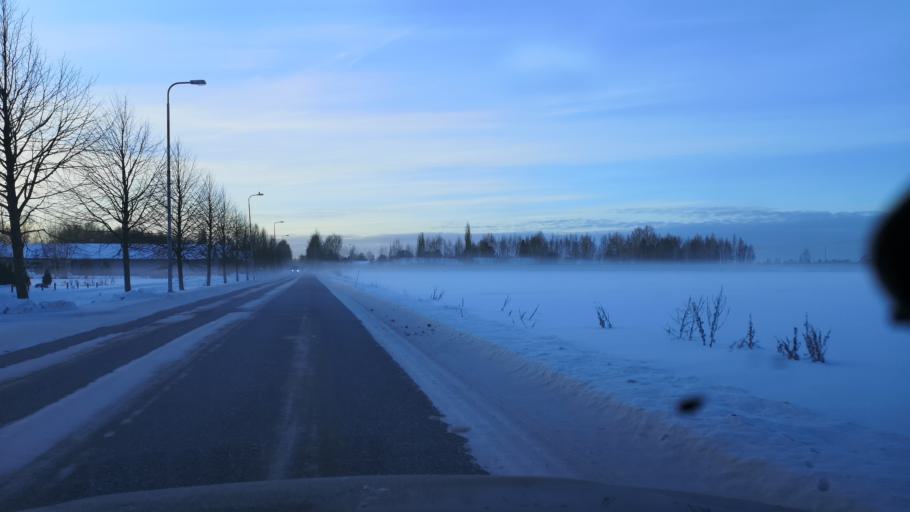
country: FI
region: Satakunta
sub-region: Pori
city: Pori
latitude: 61.5028
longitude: 21.8315
